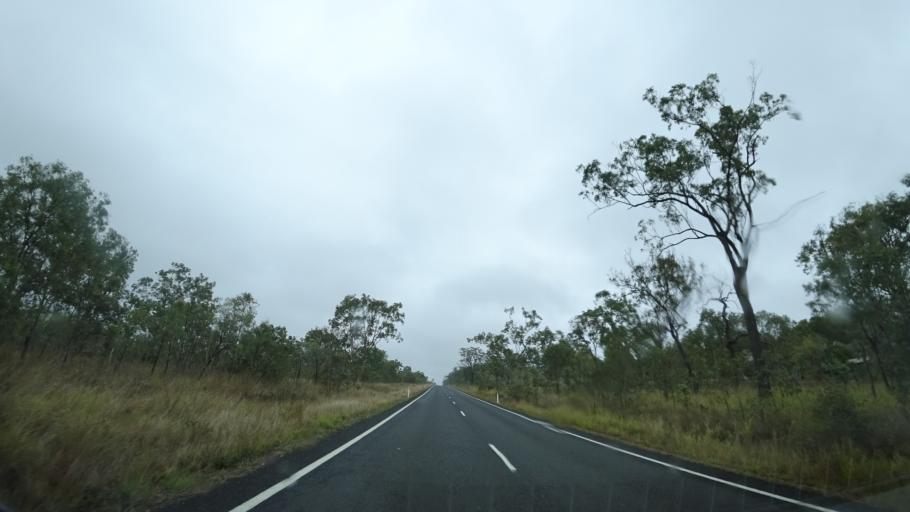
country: AU
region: Queensland
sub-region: Tablelands
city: Ravenshoe
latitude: -17.6980
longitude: 145.1901
